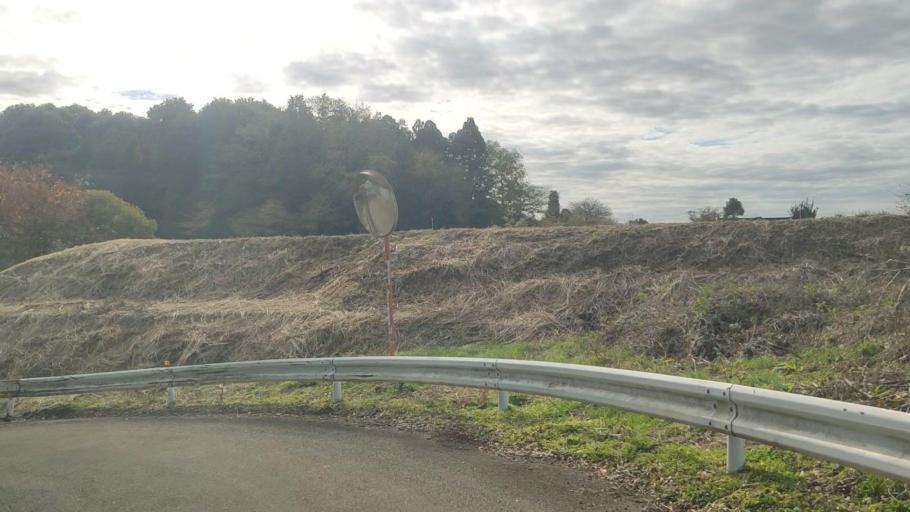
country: JP
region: Kanagawa
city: Minami-rinkan
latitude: 35.4864
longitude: 139.4980
